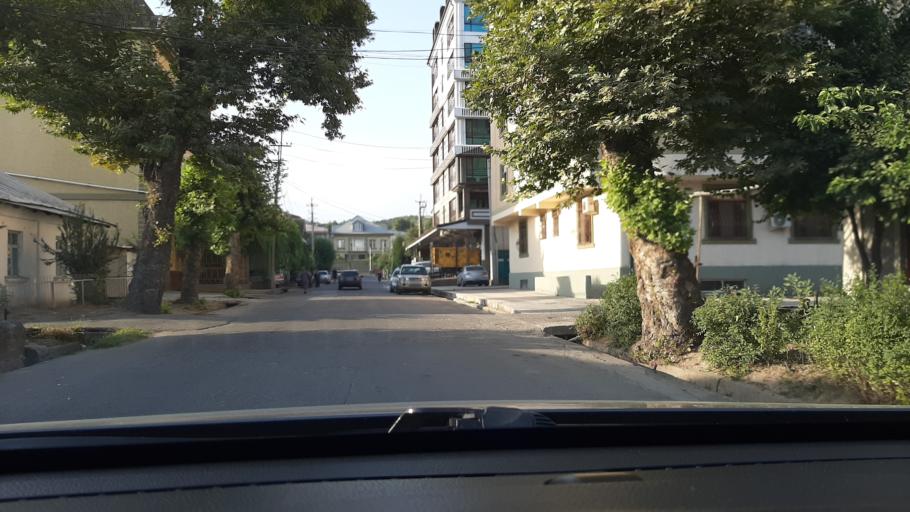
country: TJ
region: Dushanbe
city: Dushanbe
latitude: 38.5662
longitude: 68.8118
